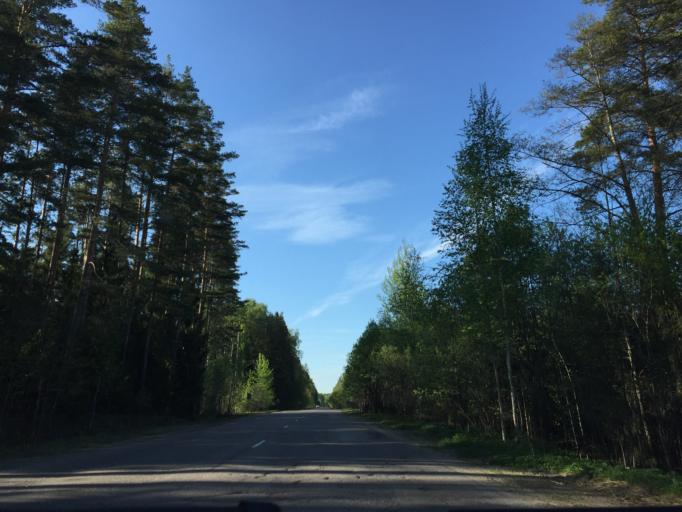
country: LV
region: Kekava
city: Balozi
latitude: 56.7404
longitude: 24.1086
